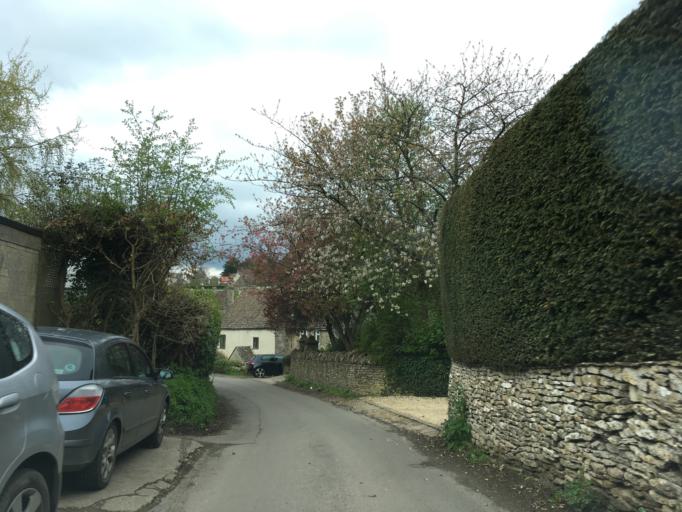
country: GB
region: England
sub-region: Gloucestershire
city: Stonehouse
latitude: 51.7006
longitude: -2.2857
